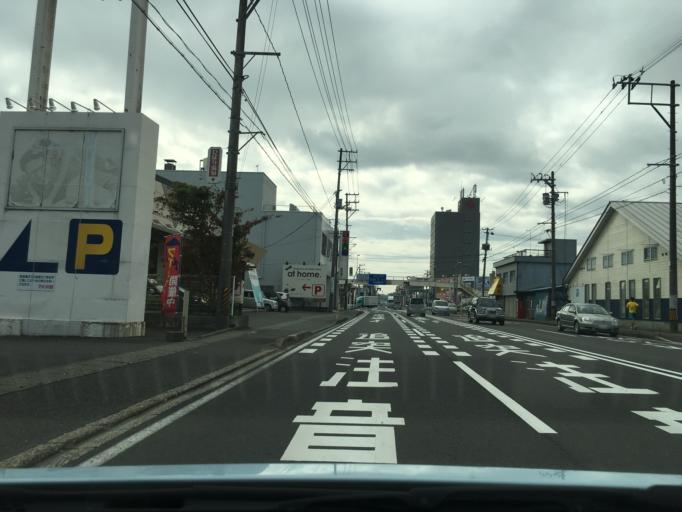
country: JP
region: Fukushima
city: Koriyama
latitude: 37.3631
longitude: 140.3686
